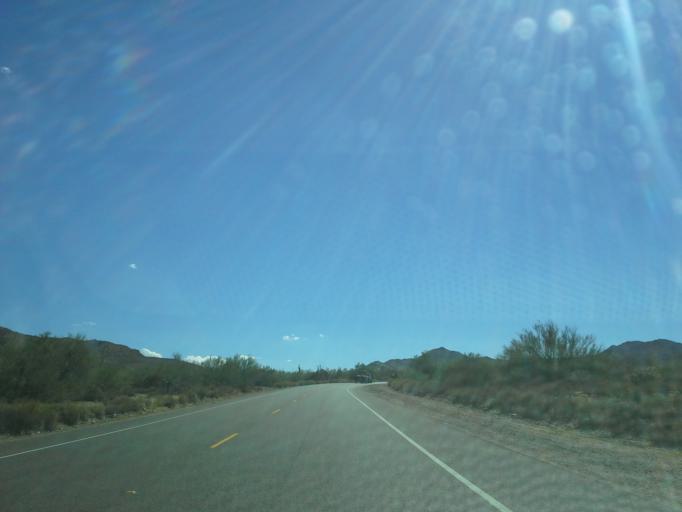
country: US
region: Arizona
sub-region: Maricopa County
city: Fountain Hills
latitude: 33.5322
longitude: -111.6116
